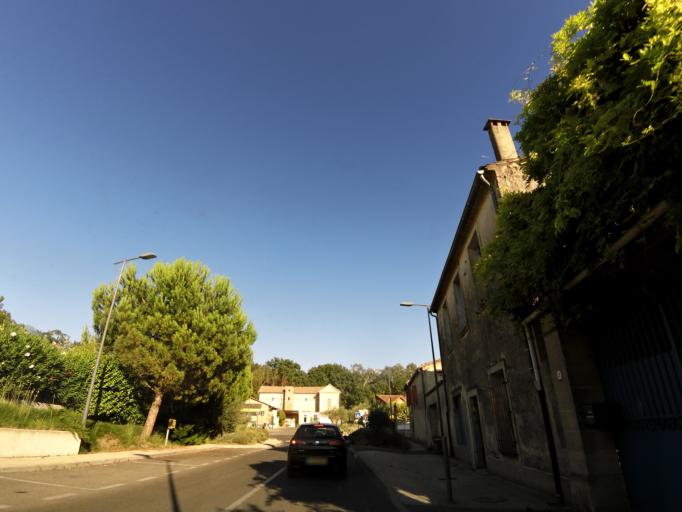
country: FR
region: Languedoc-Roussillon
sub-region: Departement du Gard
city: Sommieres
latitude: 43.7910
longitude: 4.0899
